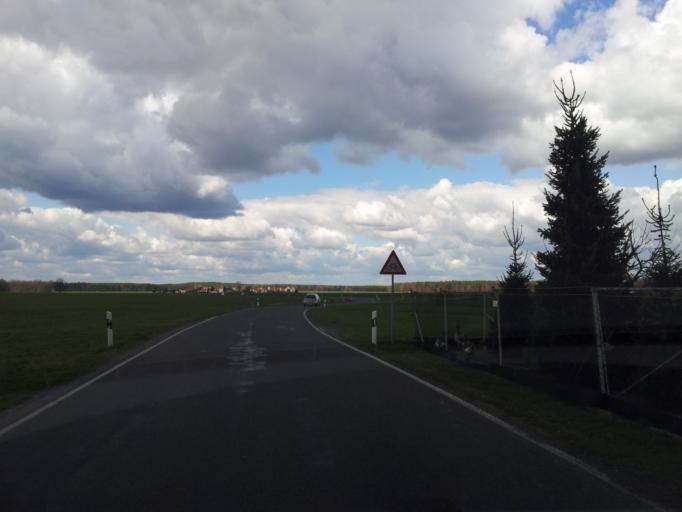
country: DE
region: Saxony
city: Horka
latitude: 51.2914
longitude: 14.2258
